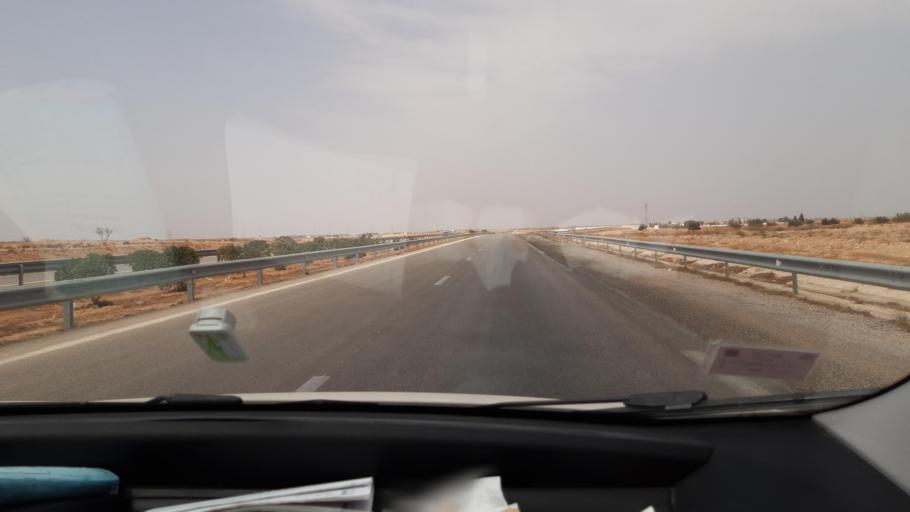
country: TN
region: Safaqis
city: Sfax
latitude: 34.7692
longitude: 10.6104
